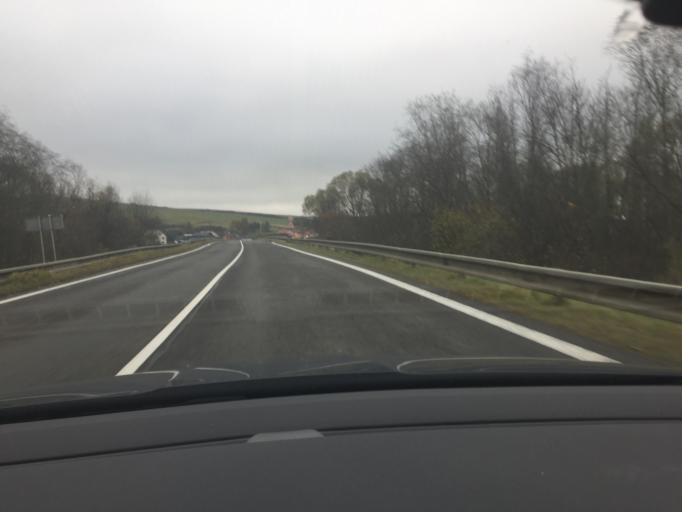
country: PL
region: Lesser Poland Voivodeship
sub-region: Powiat nowosadecki
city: Muszyna
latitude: 49.2679
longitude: 20.8687
